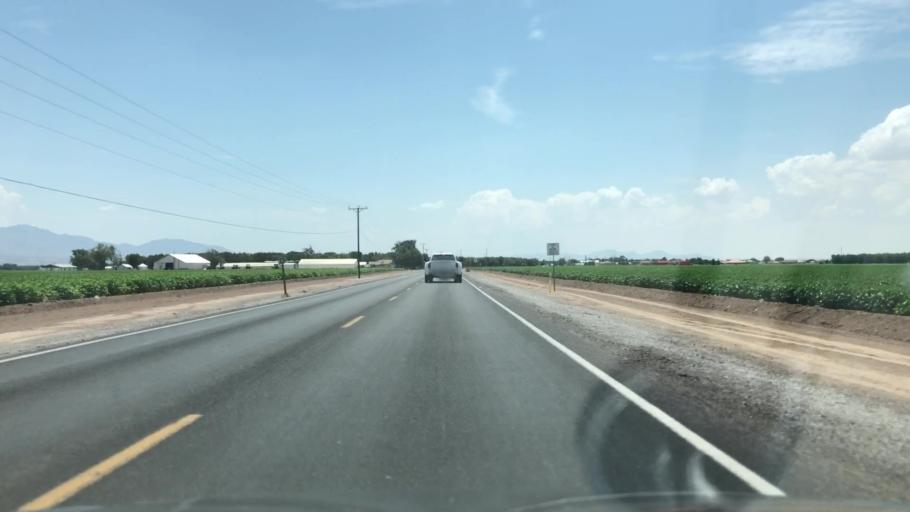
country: US
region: New Mexico
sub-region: Dona Ana County
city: La Union
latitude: 31.9670
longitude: -106.6499
